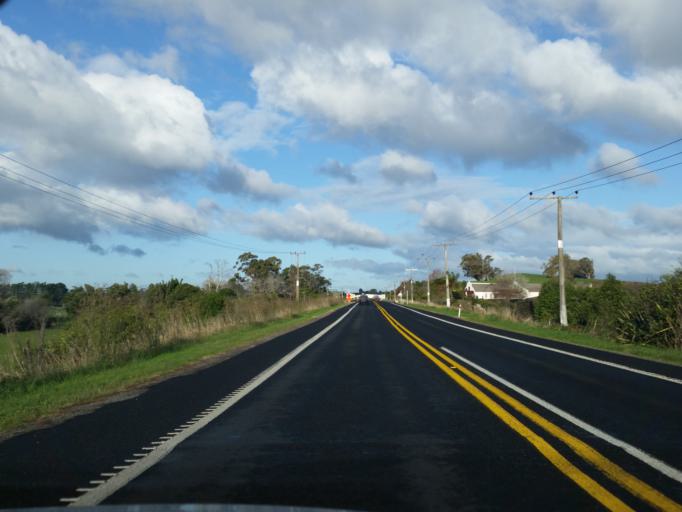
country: NZ
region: Bay of Plenty
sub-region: Western Bay of Plenty District
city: Katikati
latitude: -37.6056
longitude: 175.9391
